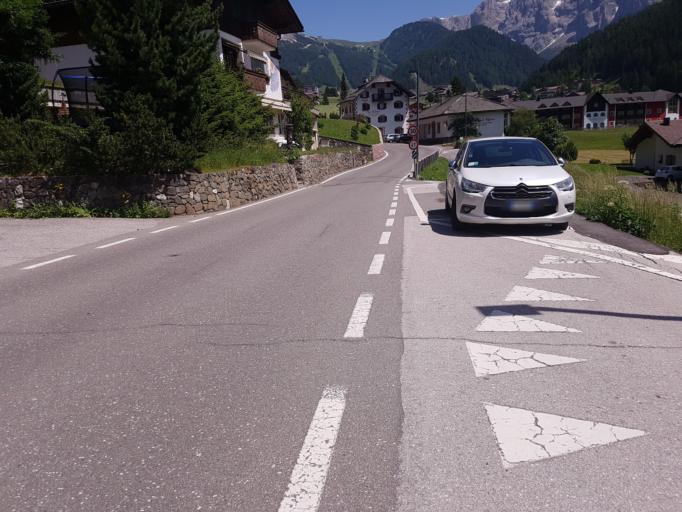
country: IT
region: Trentino-Alto Adige
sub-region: Bolzano
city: Santa Cristina Valgardena
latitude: 46.5598
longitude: 11.7432
